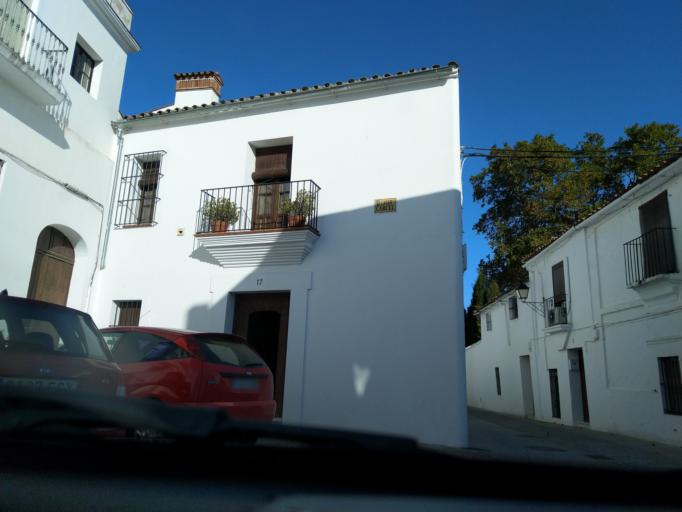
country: ES
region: Extremadura
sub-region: Provincia de Badajoz
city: Llerena
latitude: 38.2388
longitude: -6.0152
